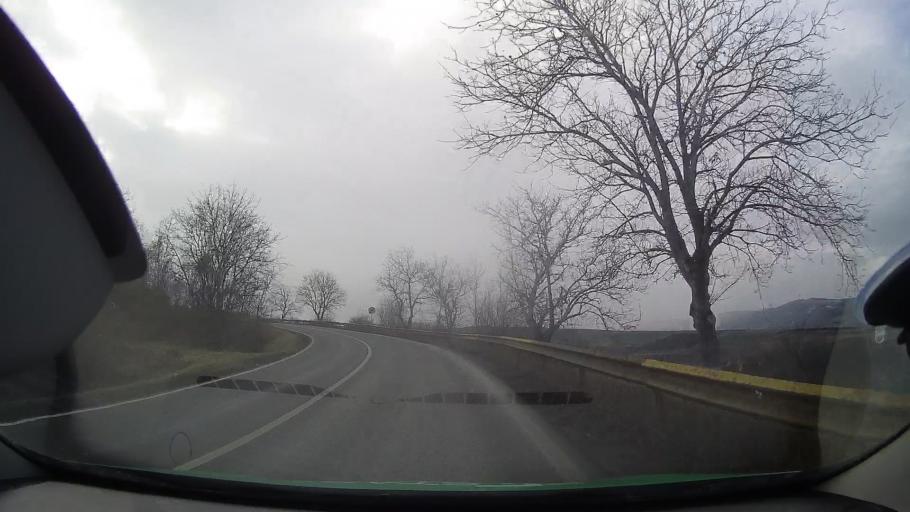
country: RO
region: Mures
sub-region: Municipiul Tarnaveni
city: Bobohalma
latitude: 46.3592
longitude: 24.2677
